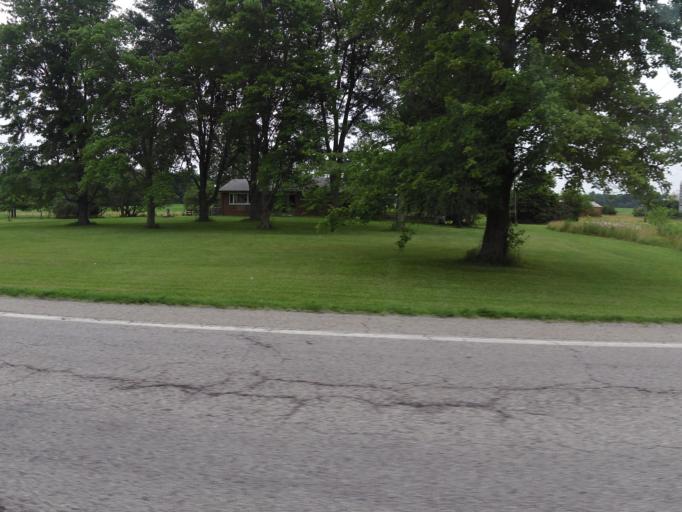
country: US
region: Ohio
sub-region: Brown County
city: Mount Orab
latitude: 39.1551
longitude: -83.9324
